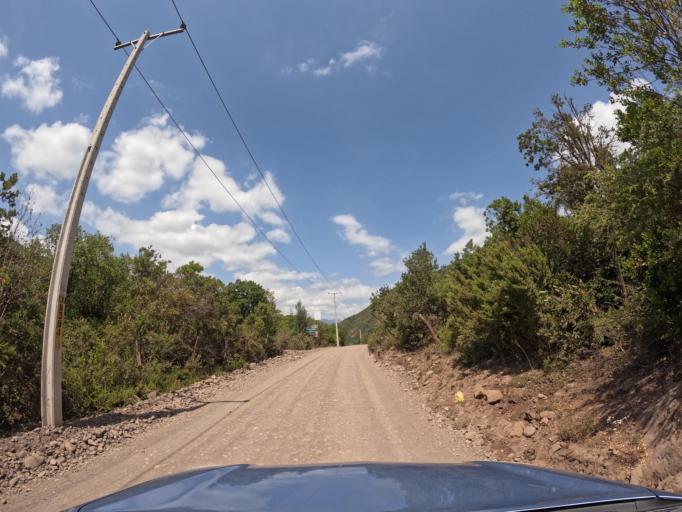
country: CL
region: Maule
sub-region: Provincia de Curico
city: Curico
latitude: -35.1249
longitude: -70.9959
